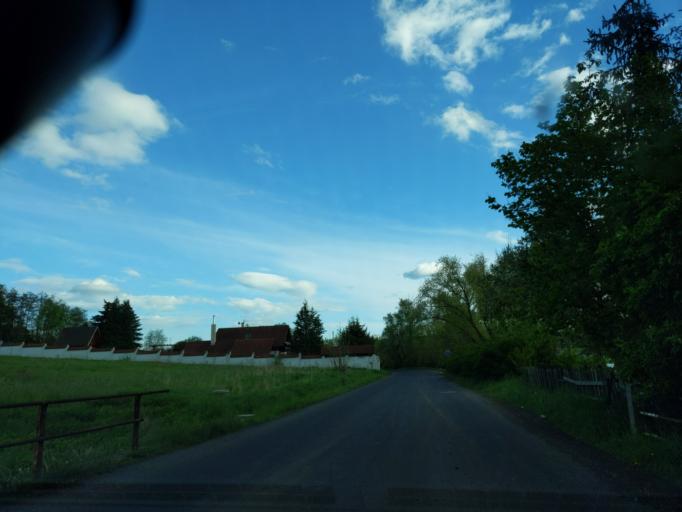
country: CZ
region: Ustecky
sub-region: Okres Usti nad Labem
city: Usti nad Labem
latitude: 50.6985
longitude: 14.0012
